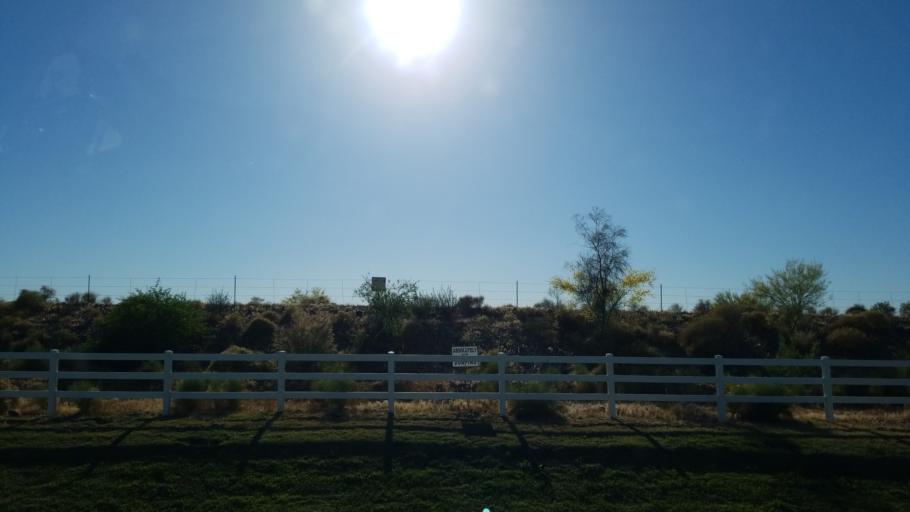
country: US
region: Arizona
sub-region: Maricopa County
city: Youngtown
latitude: 33.5716
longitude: -112.3114
